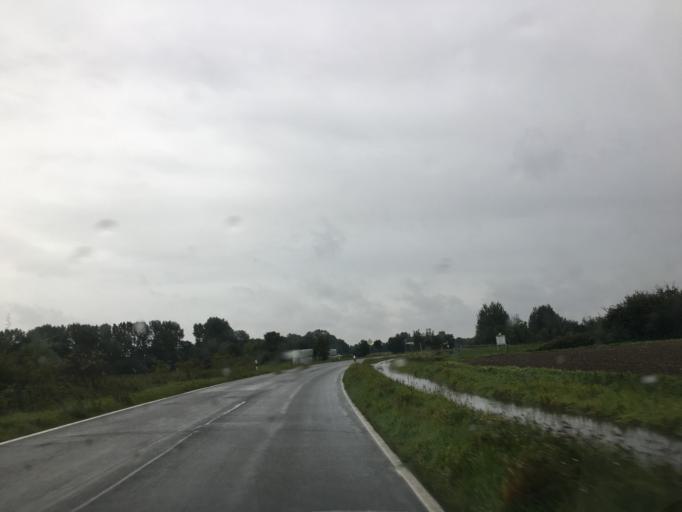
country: DE
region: Schleswig-Holstein
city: Wisch
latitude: 54.4156
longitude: 10.3766
